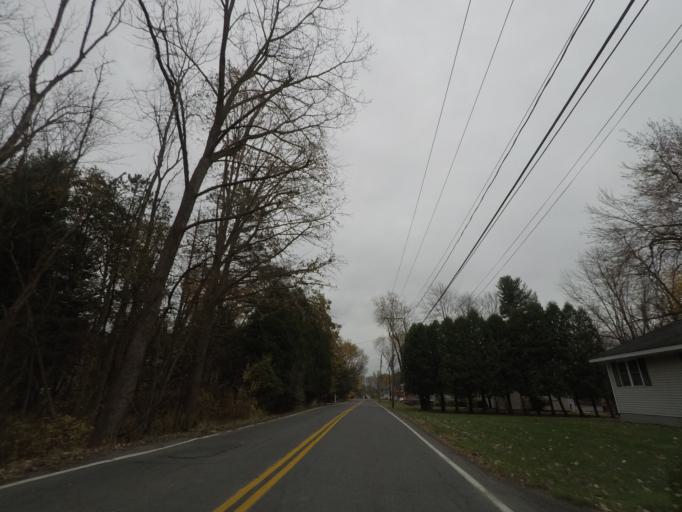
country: US
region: New York
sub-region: Albany County
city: Cohoes
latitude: 42.7963
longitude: -73.7279
